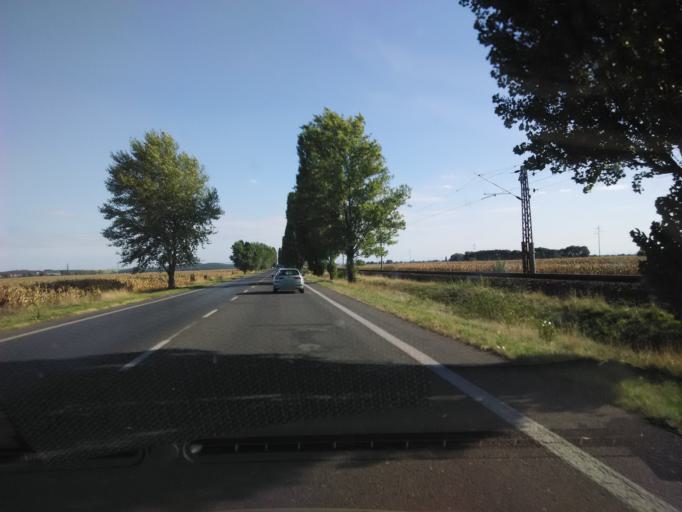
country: SK
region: Nitriansky
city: Tlmace
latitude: 48.2695
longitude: 18.5612
